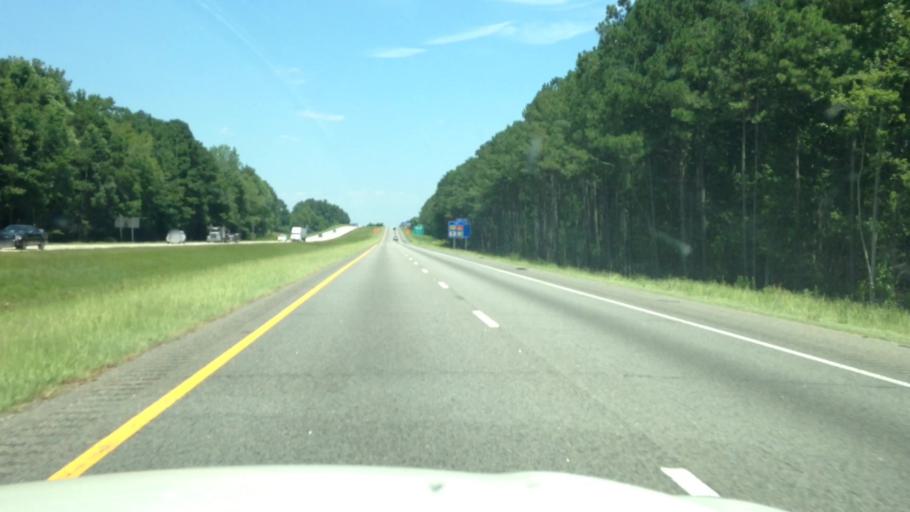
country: US
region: South Carolina
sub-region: Dillon County
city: Dillon
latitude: 34.4329
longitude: -79.3913
